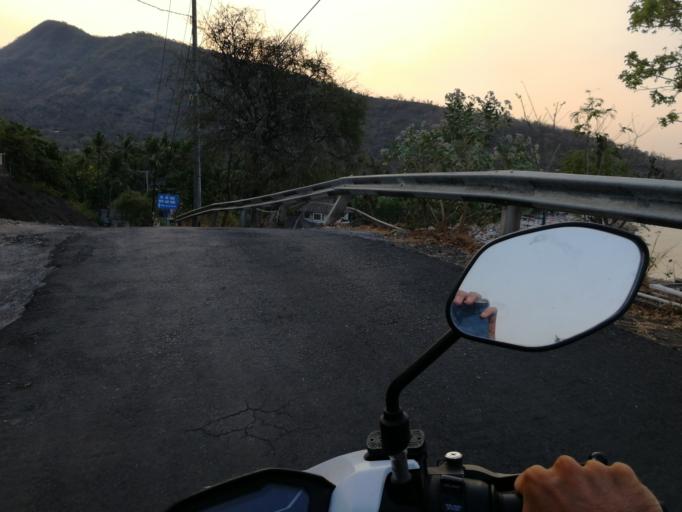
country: ID
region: Bali
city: Biaslantang Kaler
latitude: -8.3560
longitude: 115.6917
